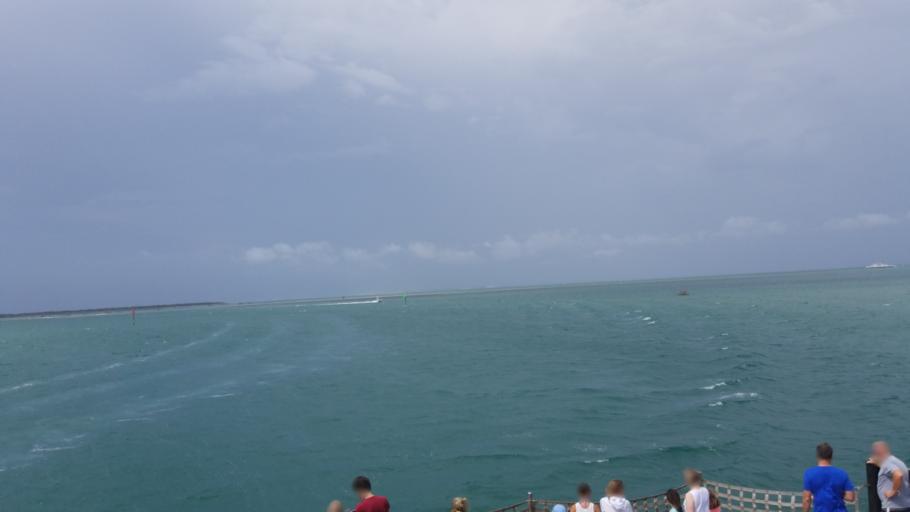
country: US
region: North Carolina
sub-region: Dare County
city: Buxton
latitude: 35.2125
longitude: -75.7162
